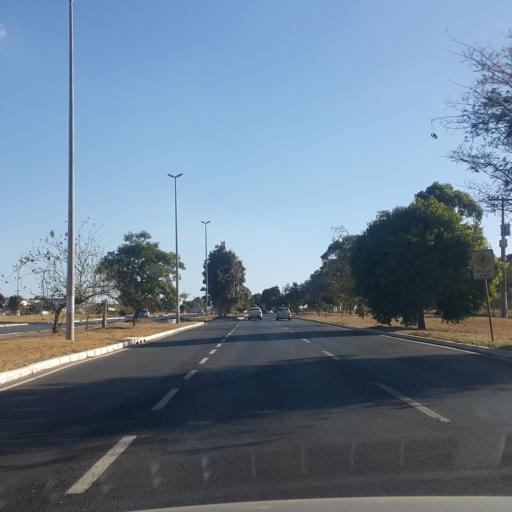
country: BR
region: Federal District
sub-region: Brasilia
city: Brasilia
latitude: -15.7947
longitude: -48.1128
